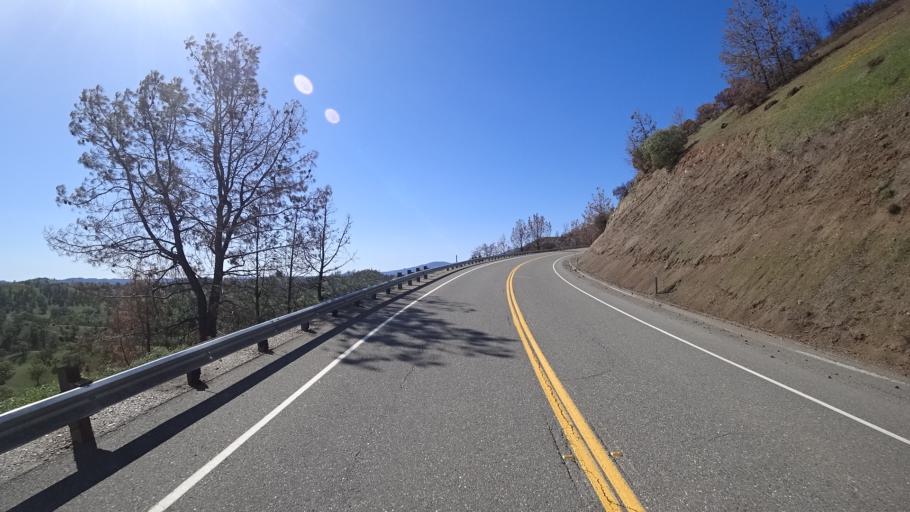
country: US
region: California
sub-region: Glenn County
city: Orland
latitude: 39.6504
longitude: -122.5939
